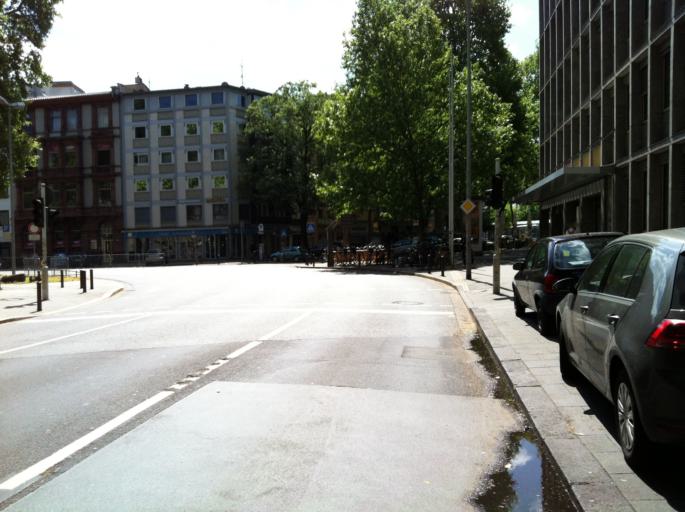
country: DE
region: Rheinland-Pfalz
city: Mainz
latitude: 50.0025
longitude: 8.2614
